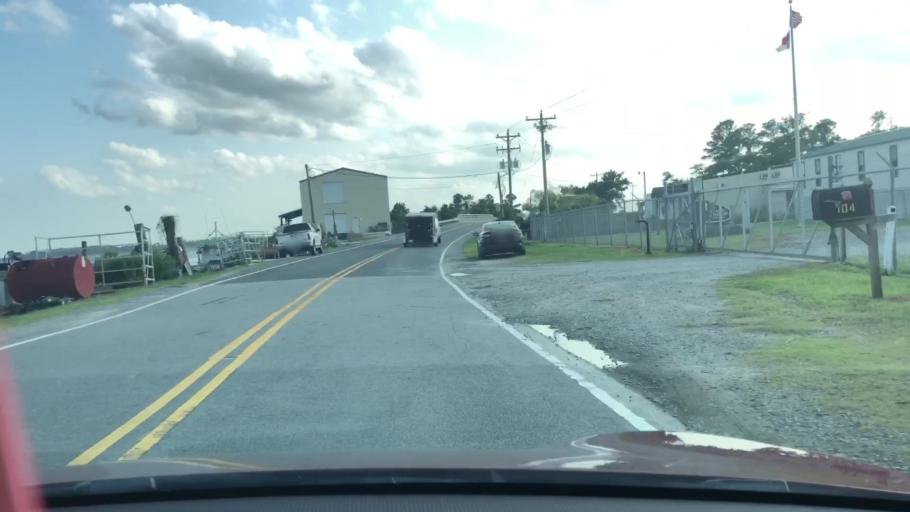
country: US
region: North Carolina
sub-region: Dare County
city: Wanchese
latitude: 35.6982
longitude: -75.7726
